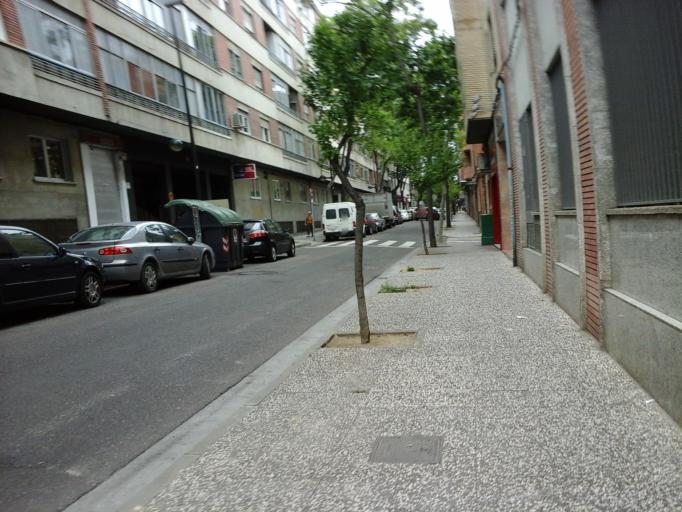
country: ES
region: Aragon
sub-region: Provincia de Zaragoza
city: Zaragoza
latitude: 41.6353
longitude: -0.8825
